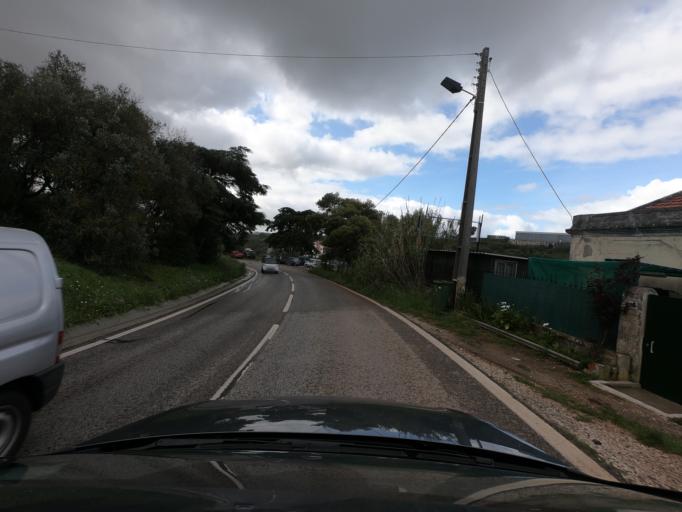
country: PT
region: Lisbon
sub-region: Sintra
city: Queluz
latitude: 38.7408
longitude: -9.2631
